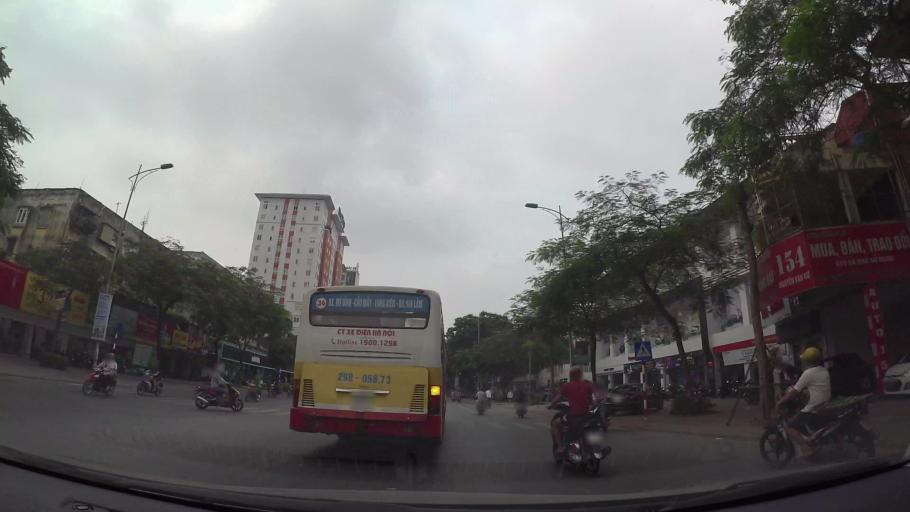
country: VN
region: Ha Noi
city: Hoan Kiem
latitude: 21.0417
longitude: 105.8699
